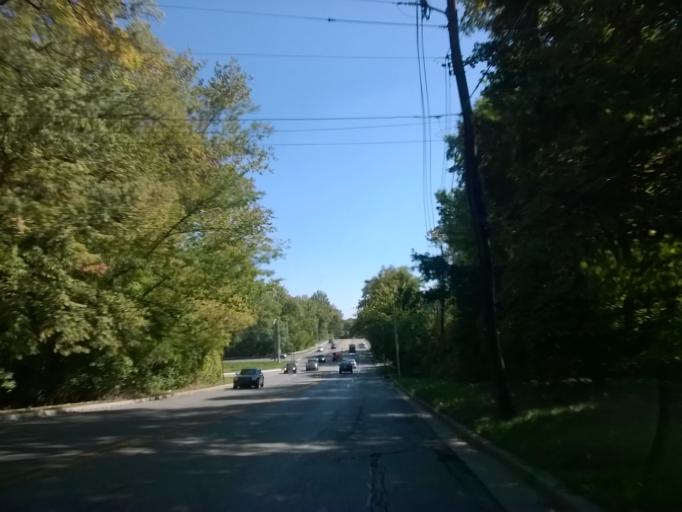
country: US
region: Indiana
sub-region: Marion County
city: Broad Ripple
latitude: 39.8623
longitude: -86.1649
